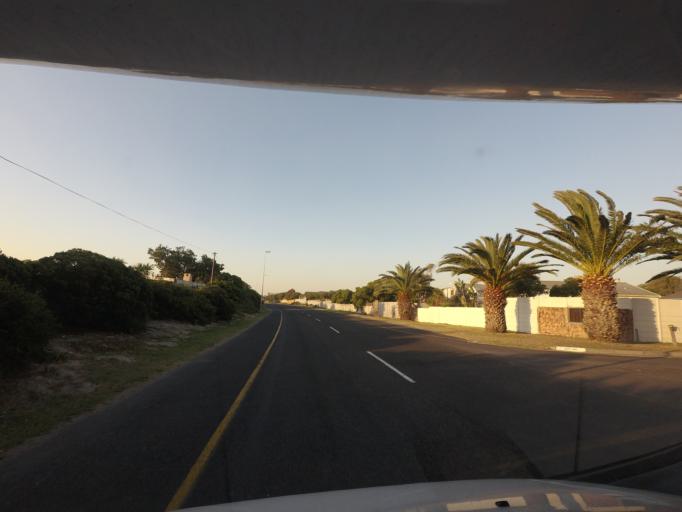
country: ZA
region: Western Cape
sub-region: City of Cape Town
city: Sunset Beach
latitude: -33.7257
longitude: 18.4477
